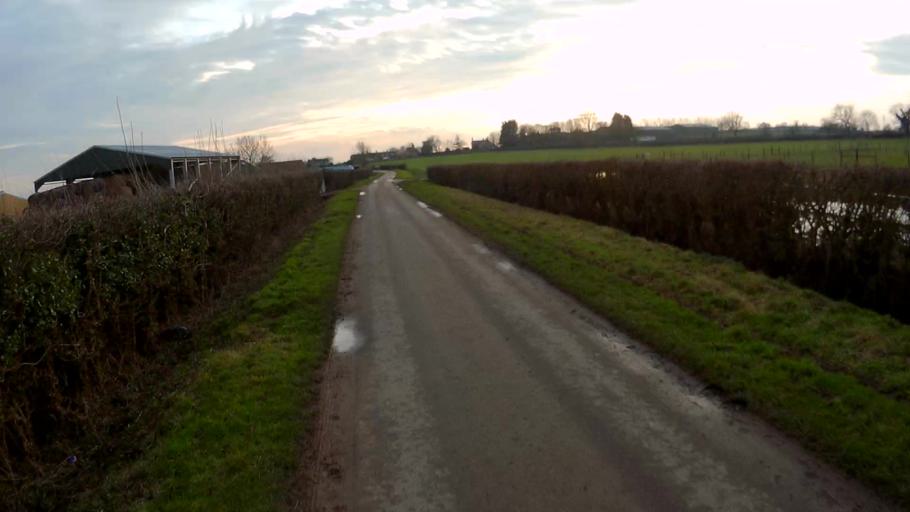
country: GB
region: England
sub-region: Lincolnshire
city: Bourne
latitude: 52.8159
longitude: -0.3984
